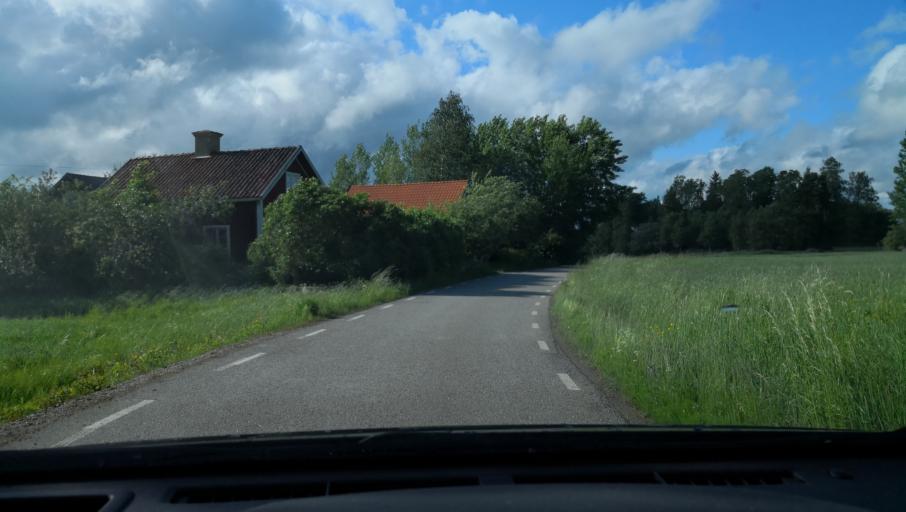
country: SE
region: OErebro
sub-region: Lindesbergs Kommun
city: Fellingsbro
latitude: 59.3370
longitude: 15.6863
